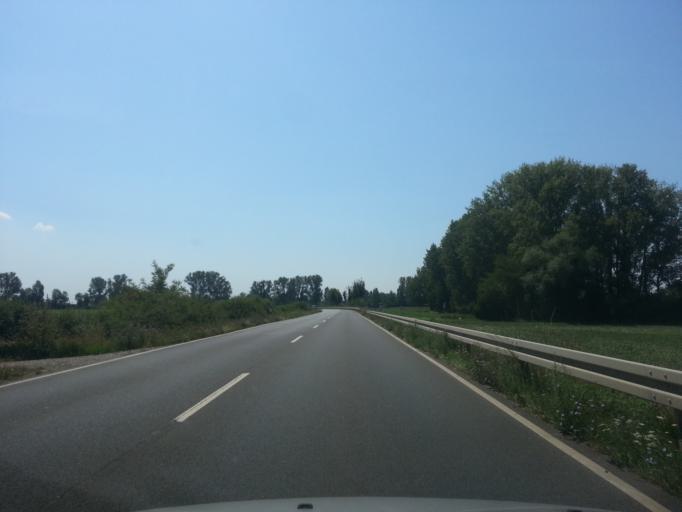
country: DE
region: Hesse
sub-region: Regierungsbezirk Darmstadt
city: Biblis
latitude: 49.6723
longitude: 8.4512
